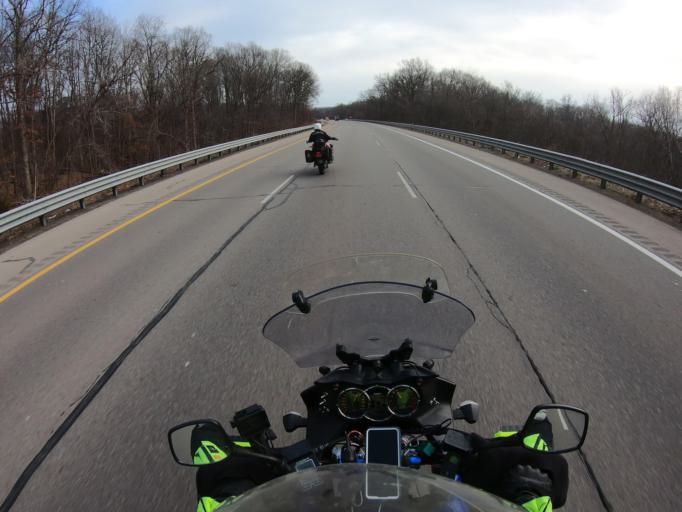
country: US
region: Michigan
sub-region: Oakland County
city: Clarkston
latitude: 42.7473
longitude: -83.4974
